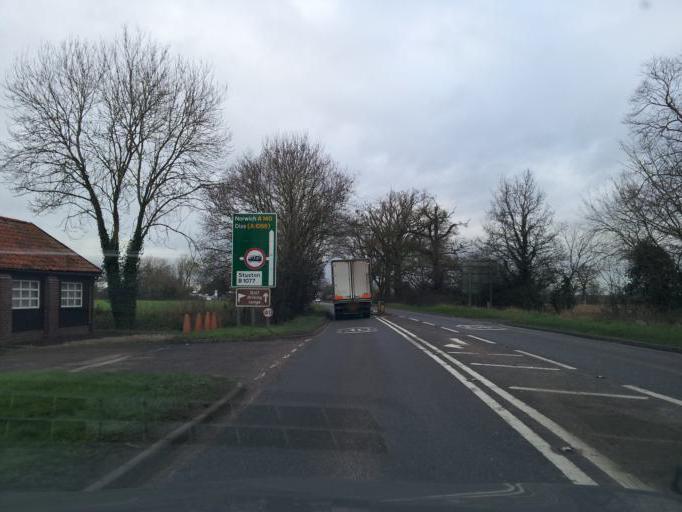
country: GB
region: England
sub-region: Norfolk
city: Diss
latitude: 52.3462
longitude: 1.1332
